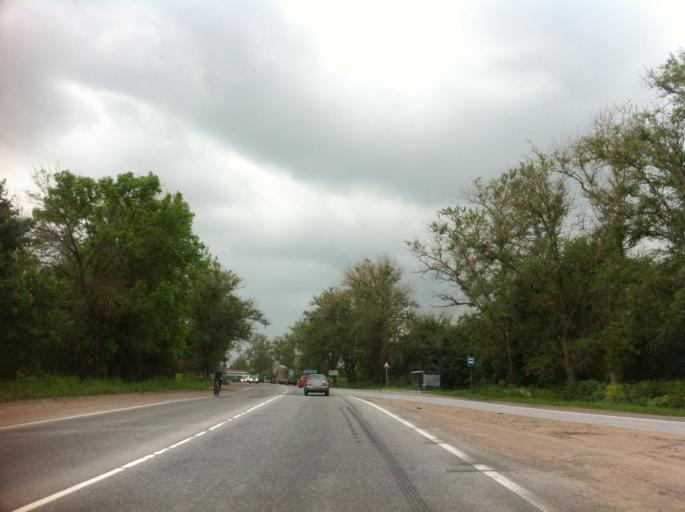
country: RU
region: Leningrad
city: Mariyenburg
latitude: 59.5230
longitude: 30.0699
